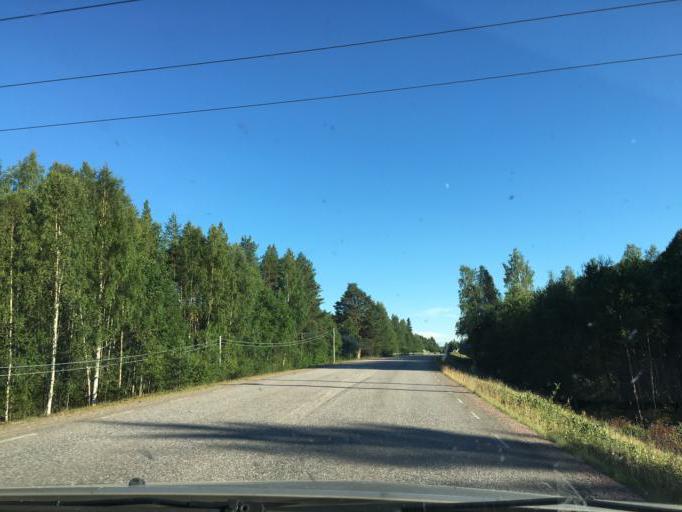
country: SE
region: Norrbotten
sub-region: Kalix Kommun
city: Rolfs
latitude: 65.9085
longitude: 22.9295
